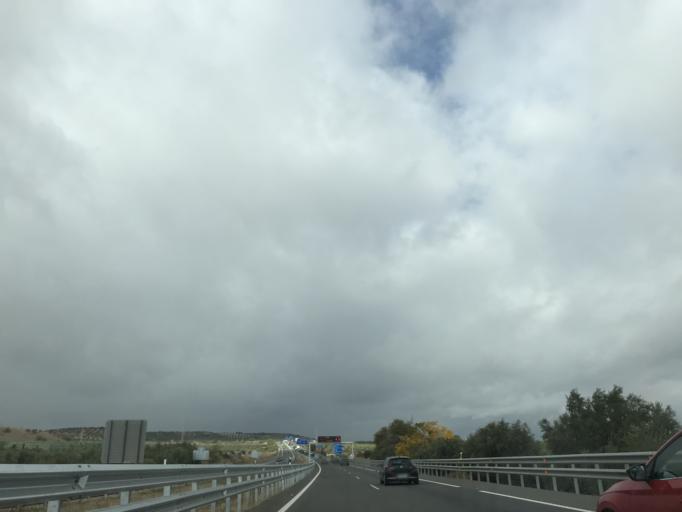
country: ES
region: Andalusia
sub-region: Provincia de Jaen
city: Bailen
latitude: 38.1111
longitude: -3.7498
